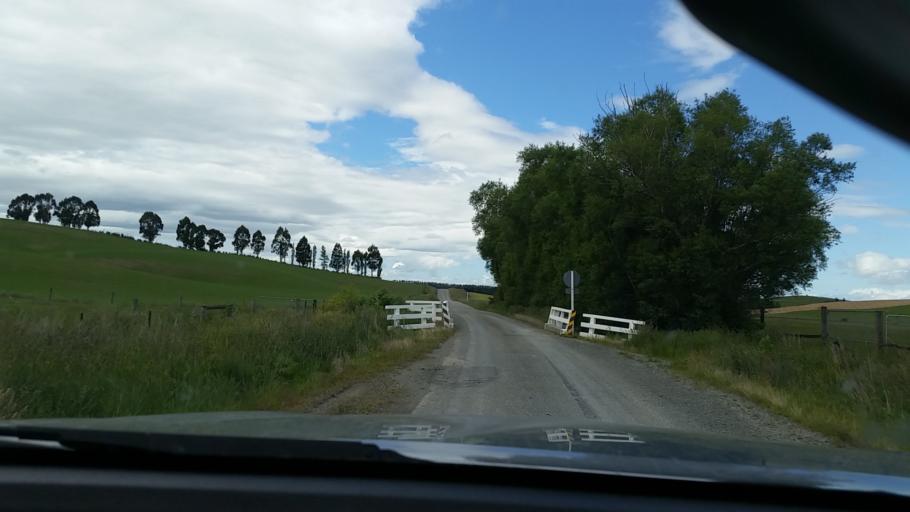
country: NZ
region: Otago
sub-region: Queenstown-Lakes District
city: Kingston
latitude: -45.7728
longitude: 168.6064
